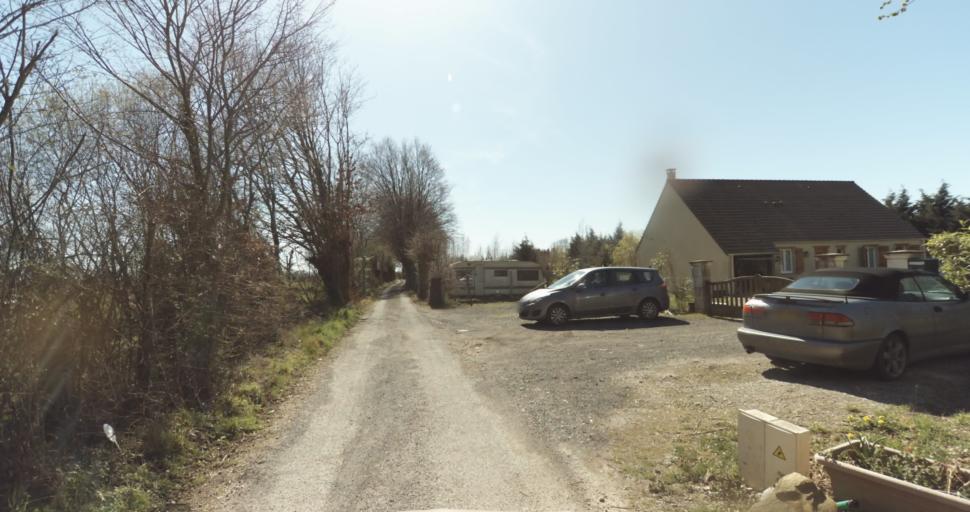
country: FR
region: Lower Normandy
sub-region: Departement du Calvados
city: Livarot
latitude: 49.0168
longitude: 0.1096
